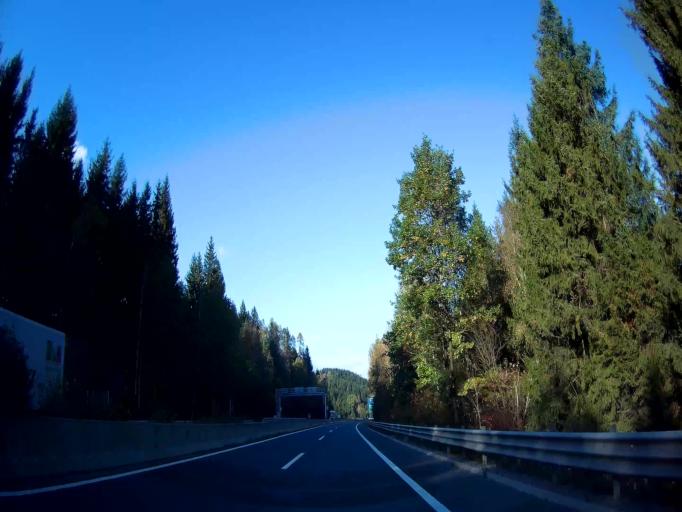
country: AT
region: Carinthia
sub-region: Politischer Bezirk Wolfsberg
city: Sankt Andrae
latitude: 46.7371
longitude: 14.8039
